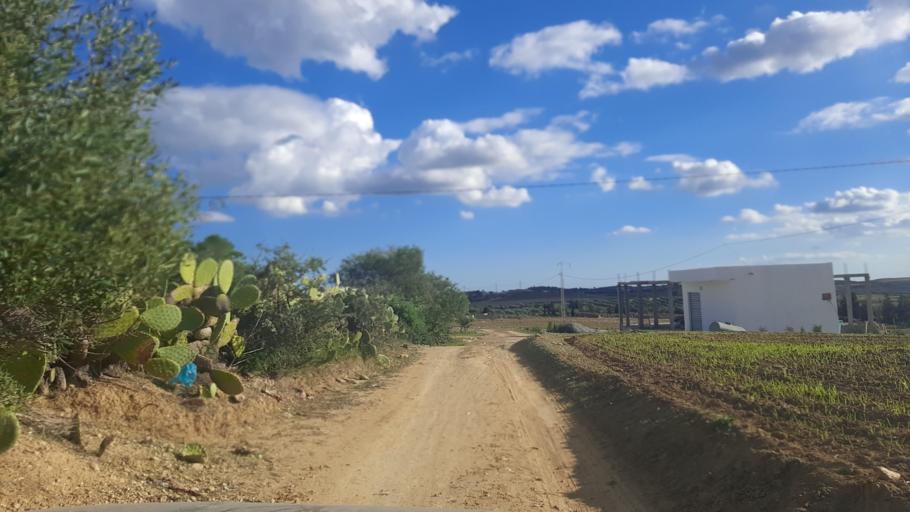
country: TN
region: Nabul
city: Bu `Urqub
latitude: 36.4560
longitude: 10.4972
